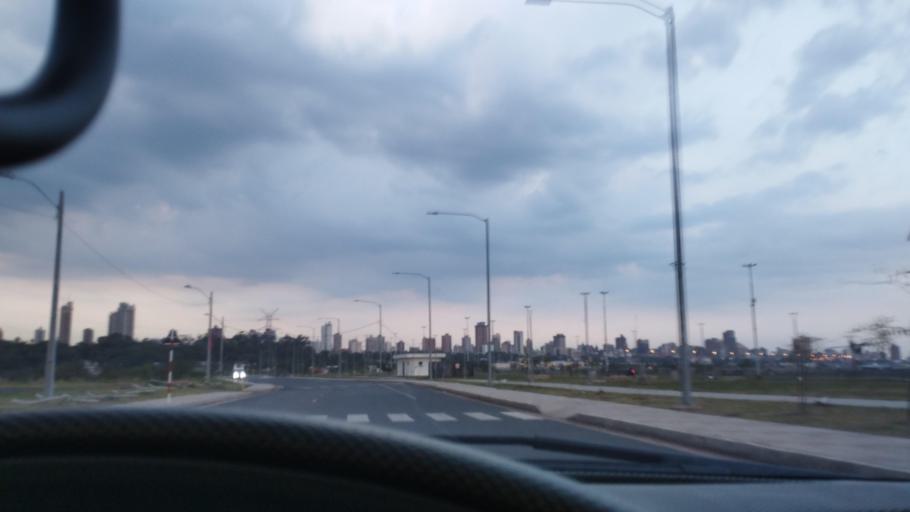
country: PY
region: Asuncion
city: Asuncion
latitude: -25.2752
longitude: -57.6162
